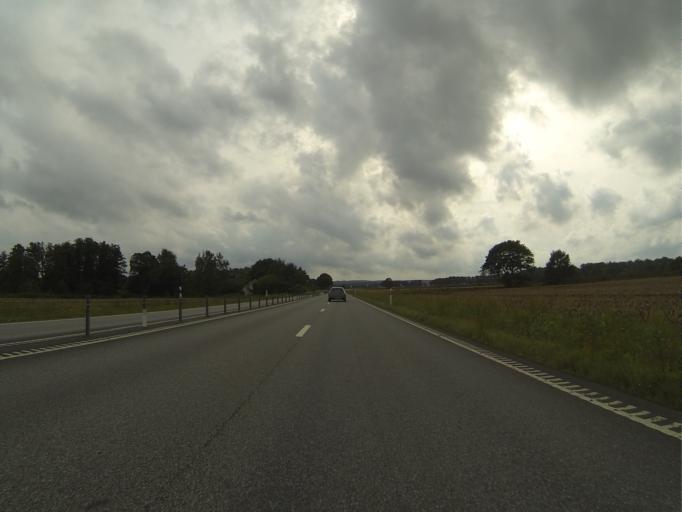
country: SE
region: Skane
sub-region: Kristianstads Kommun
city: Degeberga
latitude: 55.9386
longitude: 14.0419
